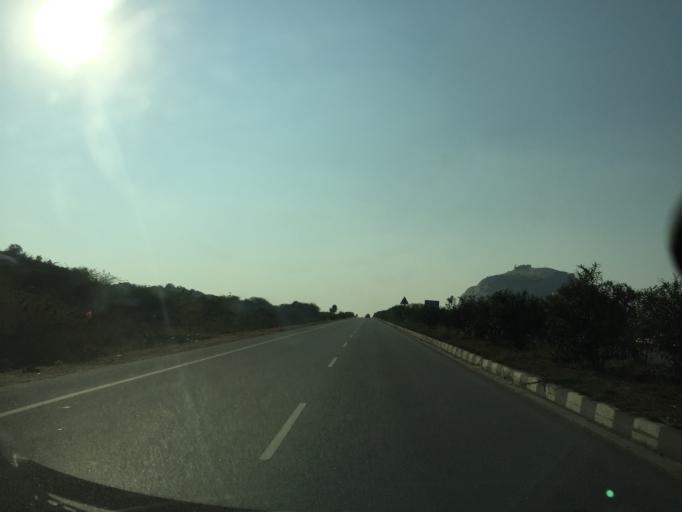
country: IN
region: Telangana
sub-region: Nalgonda
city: Bhongir
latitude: 17.5137
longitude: 78.9086
